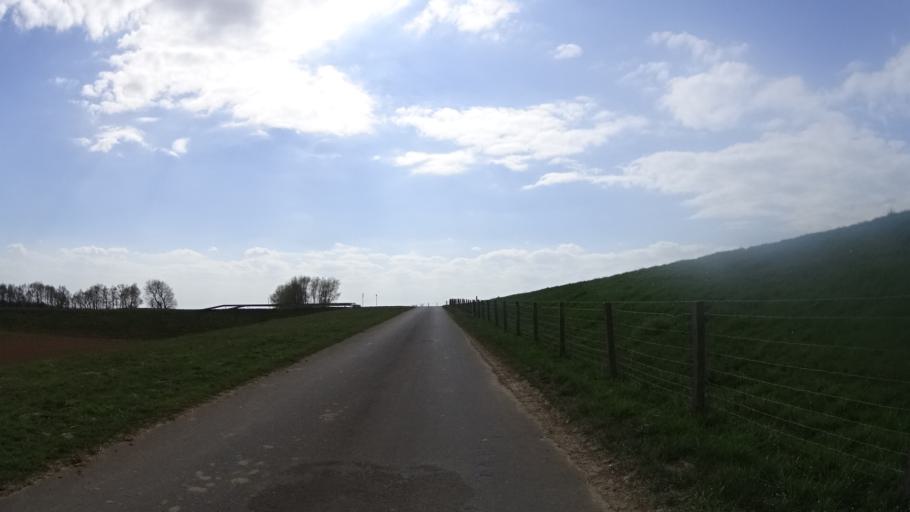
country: DE
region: Lower Saxony
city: Rhede
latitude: 53.0950
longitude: 7.2987
